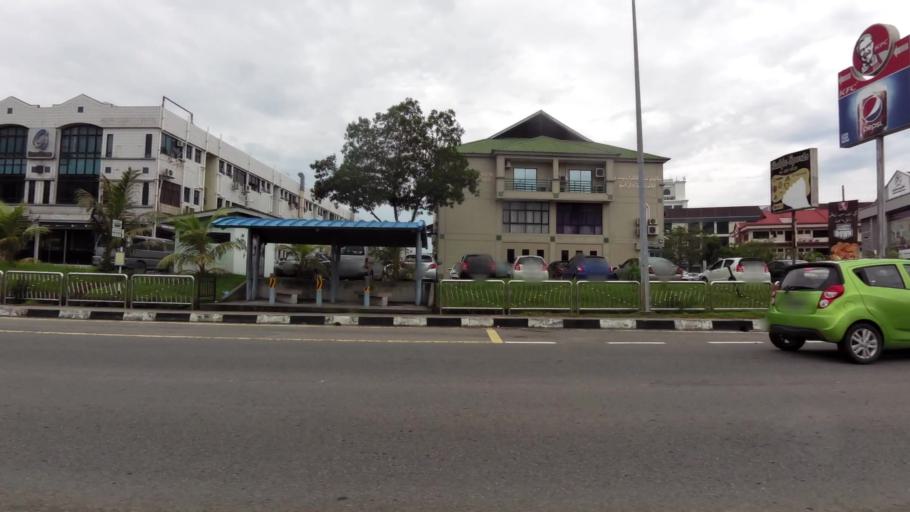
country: BN
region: Brunei and Muara
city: Bandar Seri Begawan
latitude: 4.9014
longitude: 114.9280
